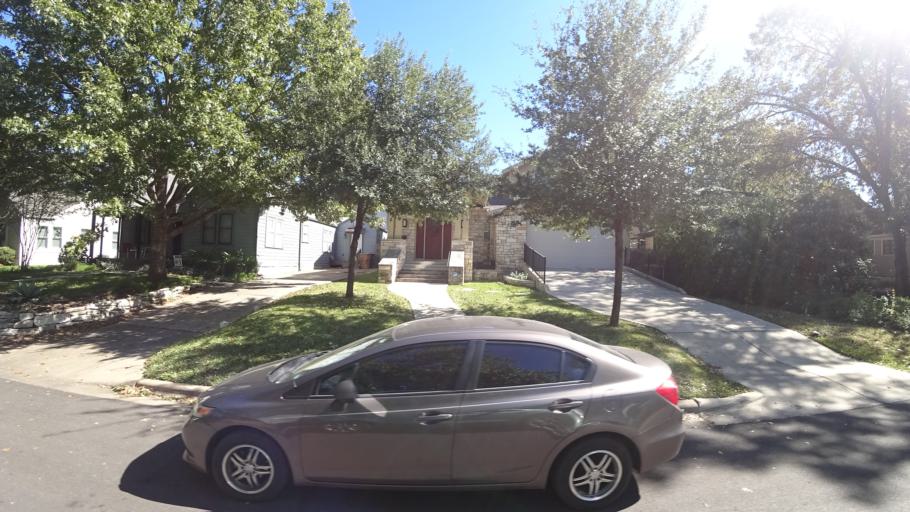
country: US
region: Texas
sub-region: Travis County
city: Austin
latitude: 30.3179
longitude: -97.7446
